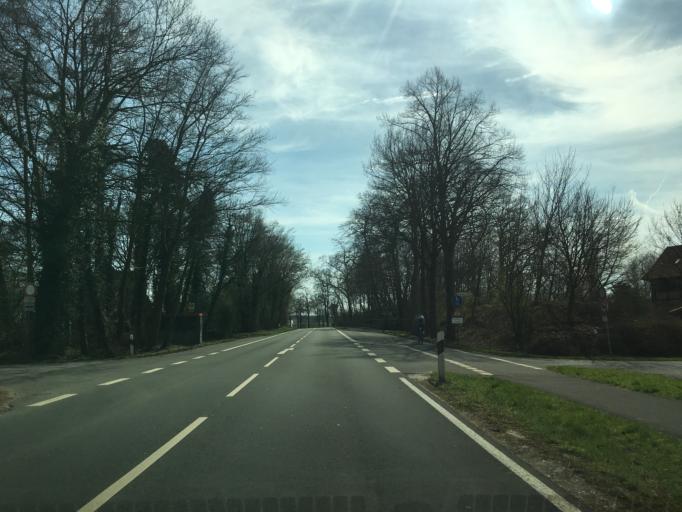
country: DE
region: North Rhine-Westphalia
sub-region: Regierungsbezirk Munster
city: Greven
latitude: 52.0729
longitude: 7.6131
